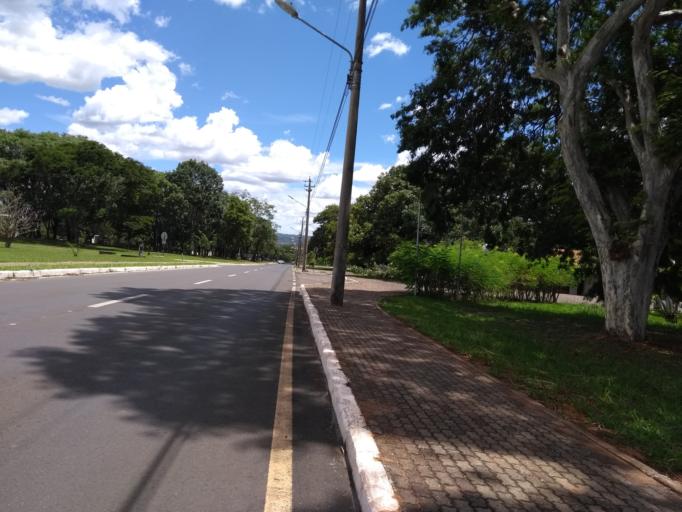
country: BR
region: Federal District
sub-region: Brasilia
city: Brasilia
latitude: -15.7696
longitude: -47.8709
